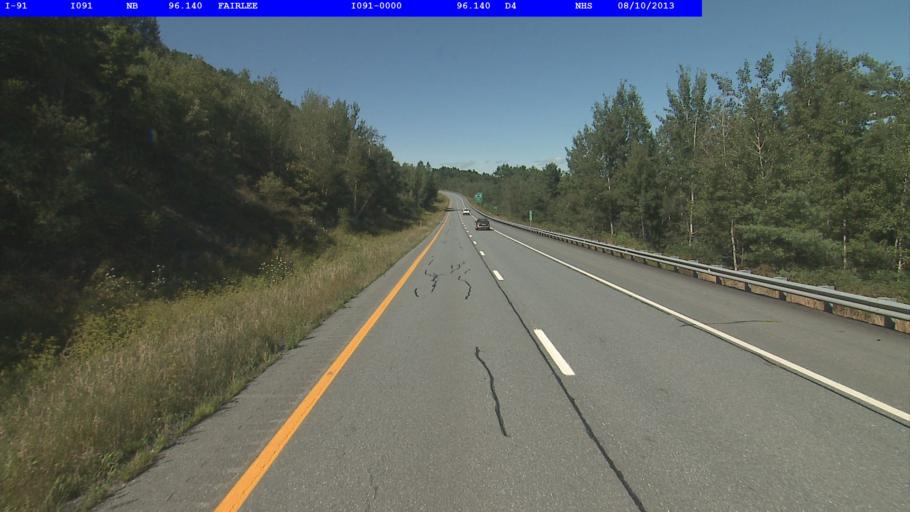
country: US
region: New Hampshire
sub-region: Grafton County
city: Orford
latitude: 43.9638
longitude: -72.1278
